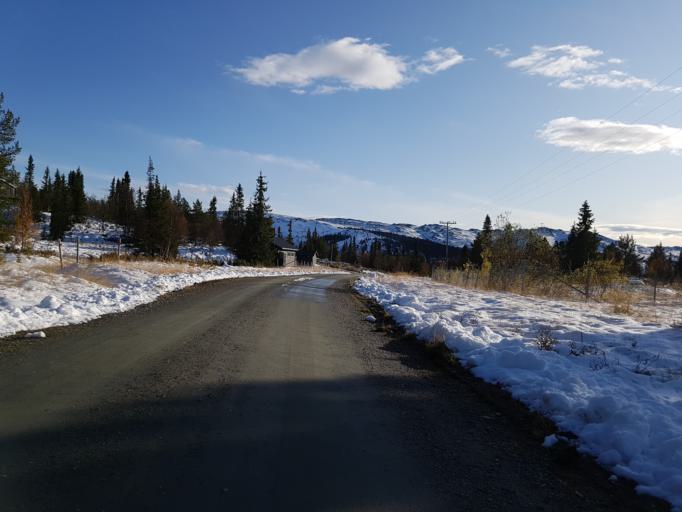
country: NO
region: Oppland
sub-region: Sel
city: Otta
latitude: 61.8180
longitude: 9.6776
